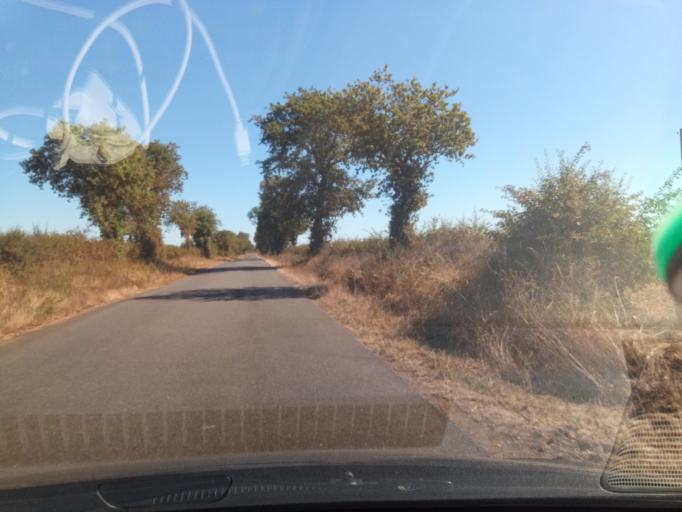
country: FR
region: Poitou-Charentes
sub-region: Departement de la Vienne
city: Saulge
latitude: 46.3802
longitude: 0.9120
